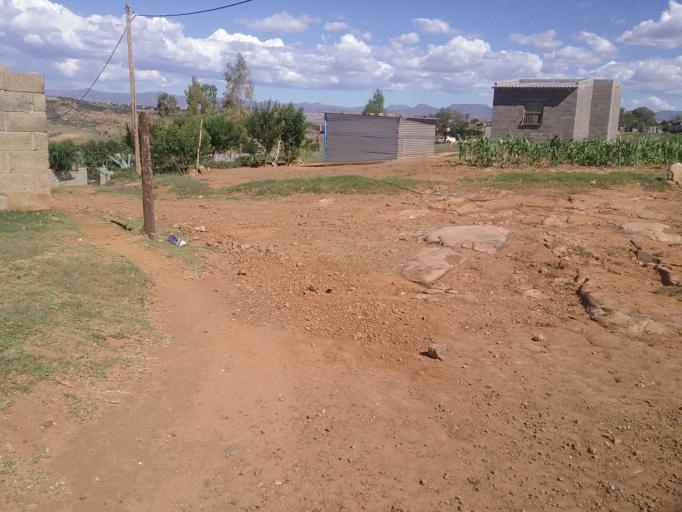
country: LS
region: Maseru
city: Maseru
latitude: -29.4168
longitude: 27.5669
